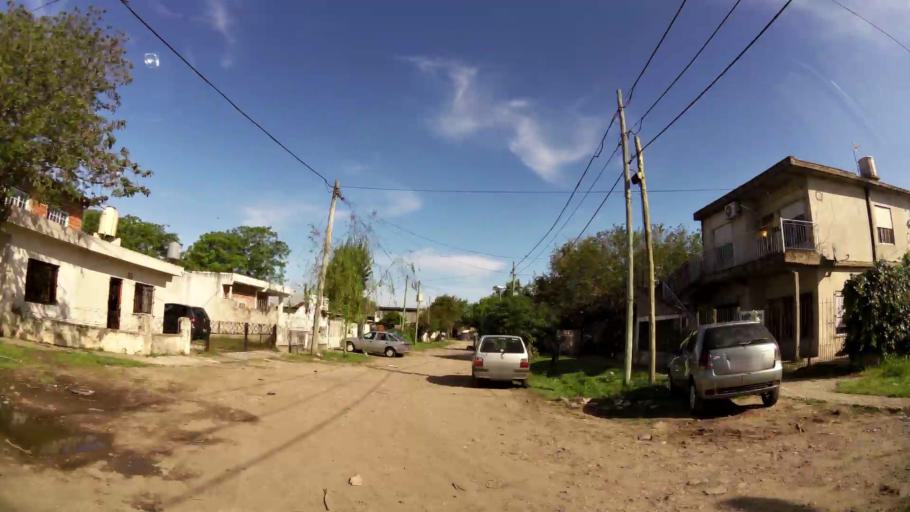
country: AR
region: Buenos Aires
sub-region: Partido de Quilmes
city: Quilmes
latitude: -34.7943
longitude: -58.2313
